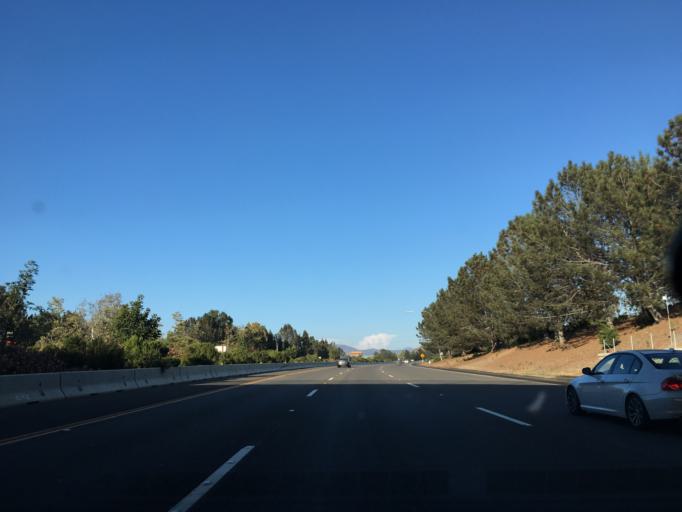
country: US
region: California
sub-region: San Diego County
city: Del Mar
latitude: 32.9372
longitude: -117.2289
